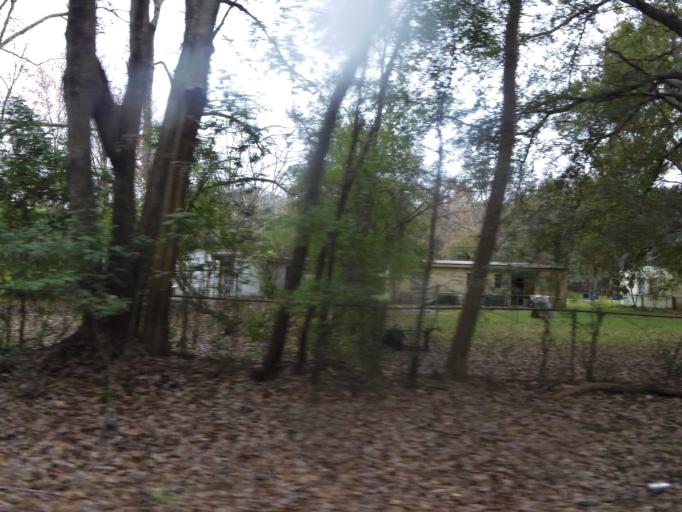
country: US
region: Florida
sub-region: Duval County
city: Jacksonville
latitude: 30.3728
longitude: -81.7014
